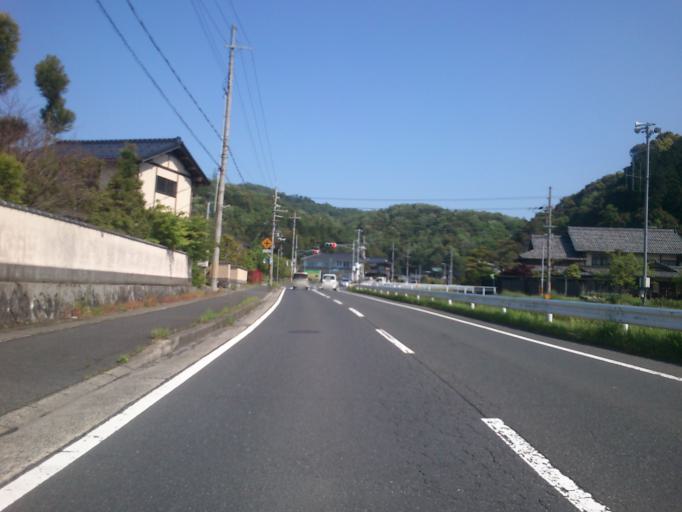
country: JP
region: Kyoto
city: Miyazu
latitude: 35.5734
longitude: 135.1609
